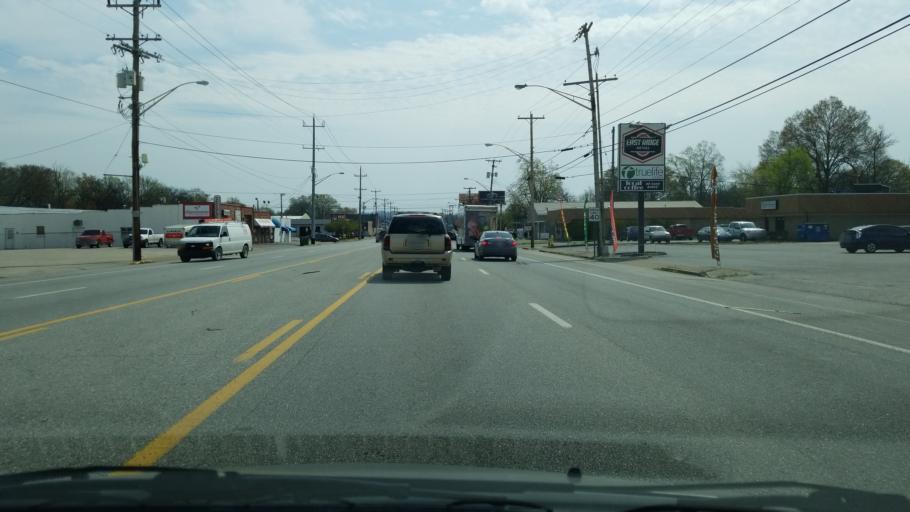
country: US
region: Tennessee
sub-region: Hamilton County
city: East Ridge
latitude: 34.9945
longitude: -85.2329
